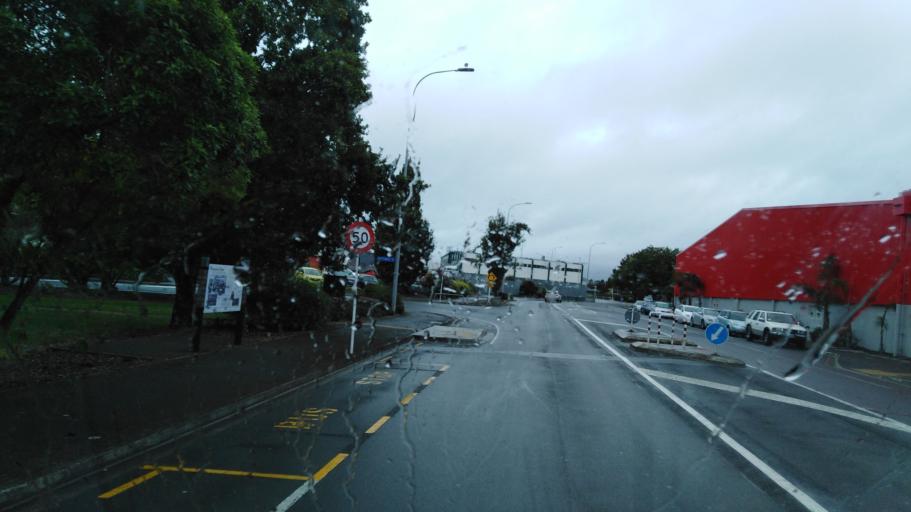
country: NZ
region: Nelson
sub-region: Nelson City
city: Nelson
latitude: -41.2719
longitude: 173.2778
